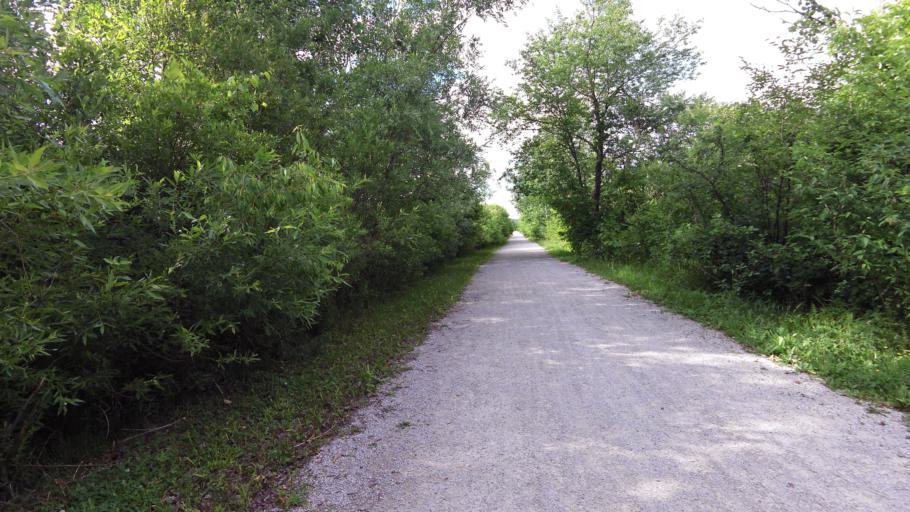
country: CA
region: Ontario
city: Brampton
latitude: 43.8014
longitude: -79.9319
